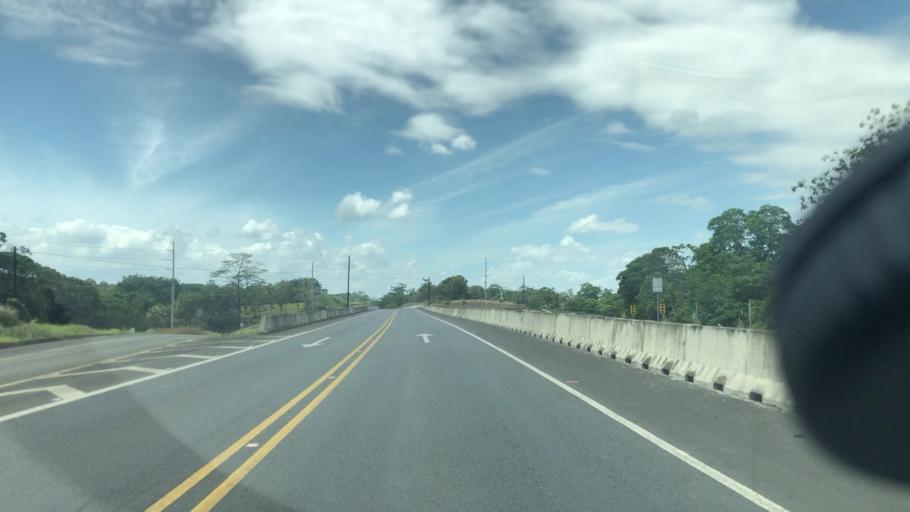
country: CR
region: Heredia
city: La Virgen
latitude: 10.4407
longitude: -84.1580
